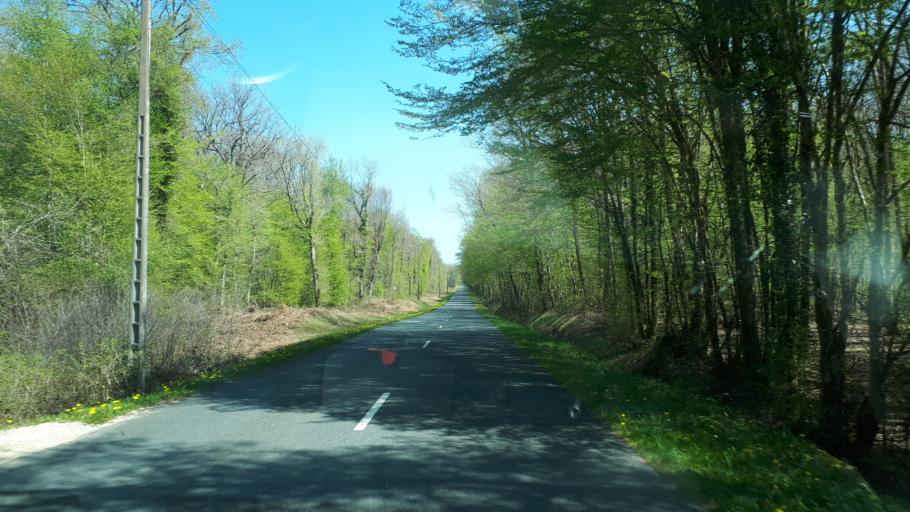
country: FR
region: Centre
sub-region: Departement du Cher
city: Henrichemont
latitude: 47.2897
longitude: 2.5962
